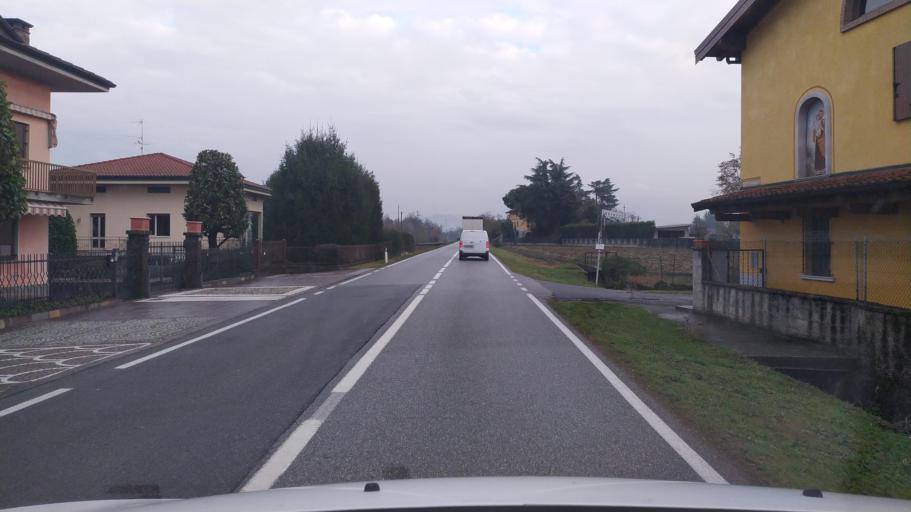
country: IT
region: Lombardy
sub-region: Provincia di Brescia
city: Pontoglio
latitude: 45.5541
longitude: 9.8580
